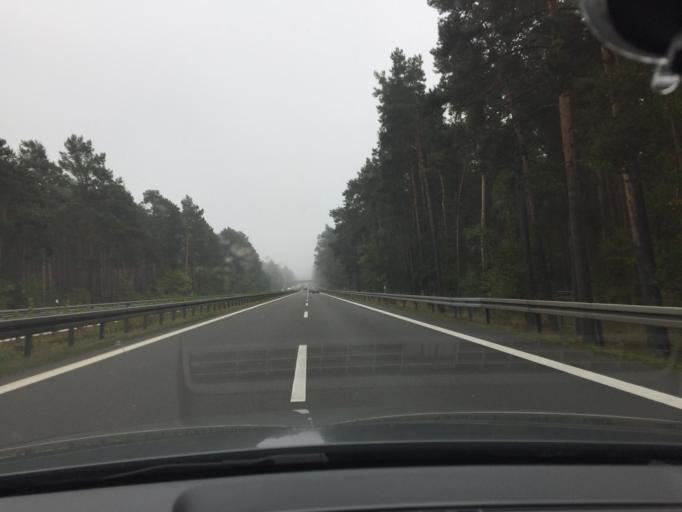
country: DE
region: Brandenburg
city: Bronkow
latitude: 51.7256
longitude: 13.8788
